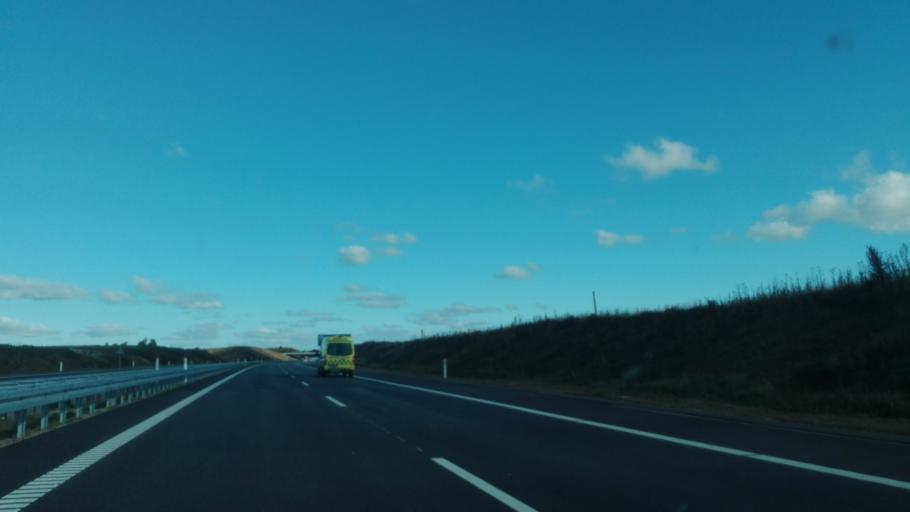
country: DK
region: Central Jutland
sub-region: Silkeborg Kommune
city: Silkeborg
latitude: 56.1961
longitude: 9.5044
